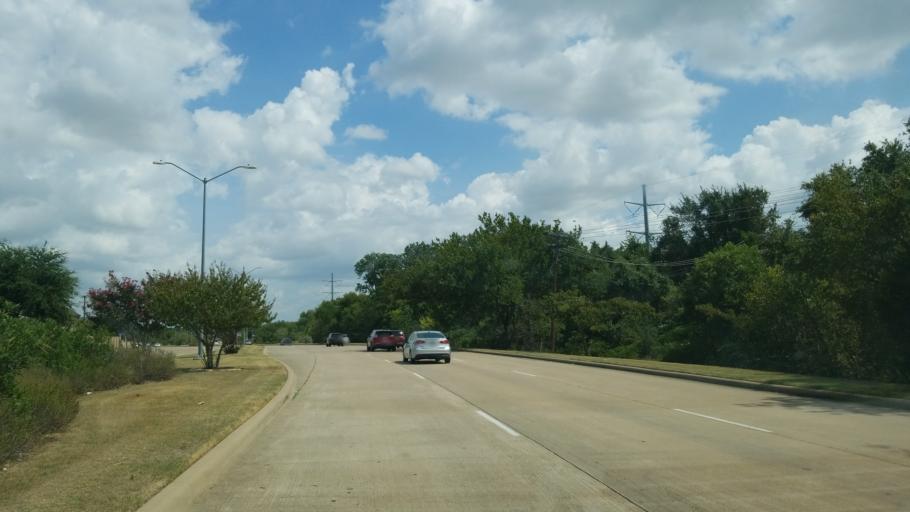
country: US
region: Texas
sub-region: Tarrant County
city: Euless
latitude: 32.8684
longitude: -97.0898
